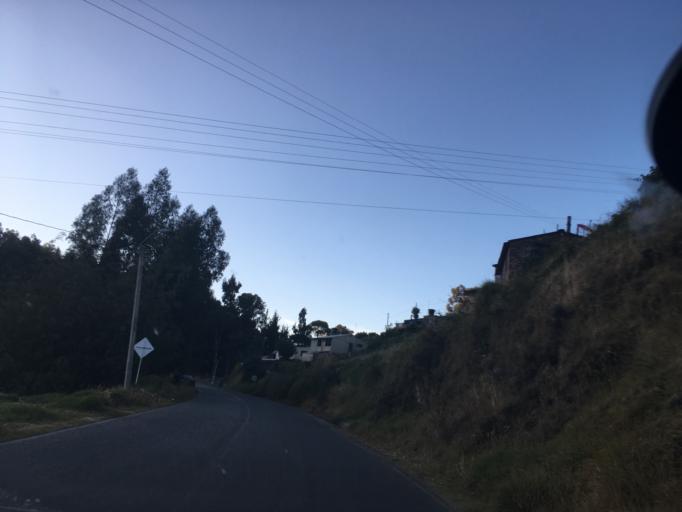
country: CO
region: Boyaca
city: Aquitania
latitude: 5.5427
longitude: -72.8830
